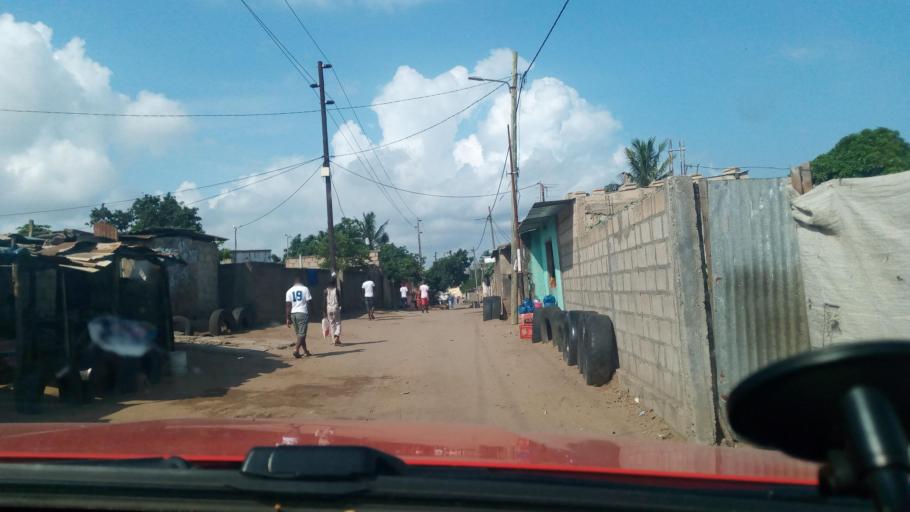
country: MZ
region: Maputo City
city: Maputo
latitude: -25.9195
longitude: 32.5621
